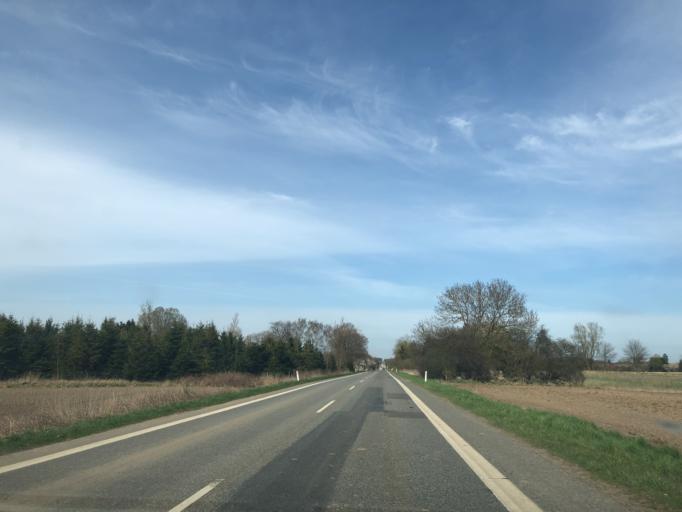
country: DK
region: Zealand
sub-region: Faxe Kommune
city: Ronnede
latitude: 55.2944
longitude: 12.0414
